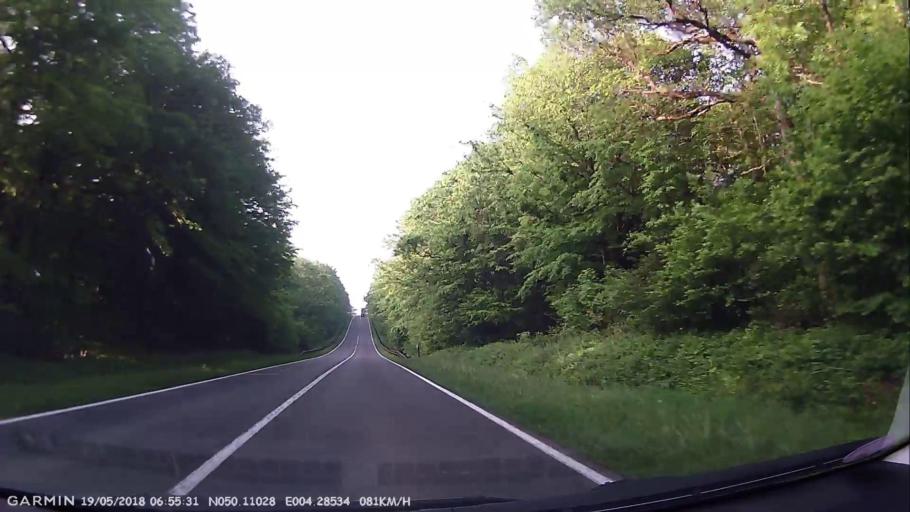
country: BE
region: Wallonia
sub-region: Province du Hainaut
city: Froidchapelle
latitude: 50.1101
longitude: 4.2854
